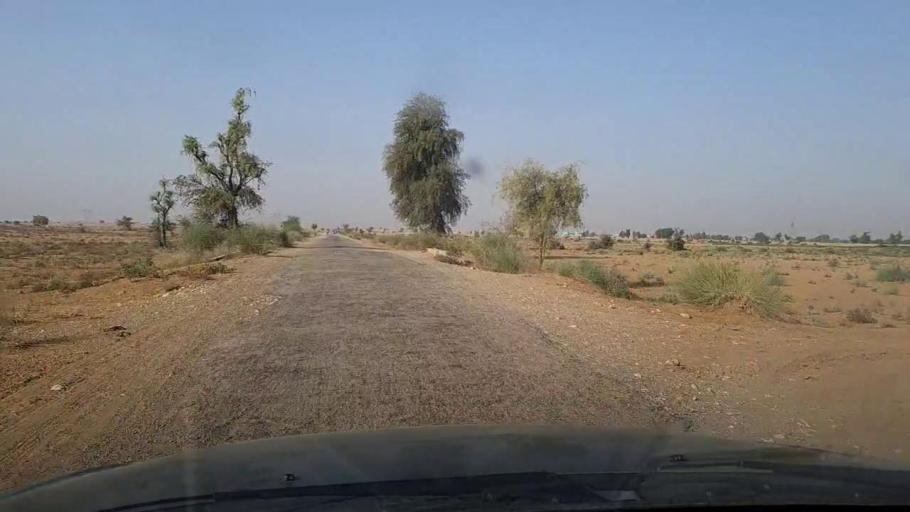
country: PK
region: Sindh
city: Sann
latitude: 26.0156
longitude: 68.0959
